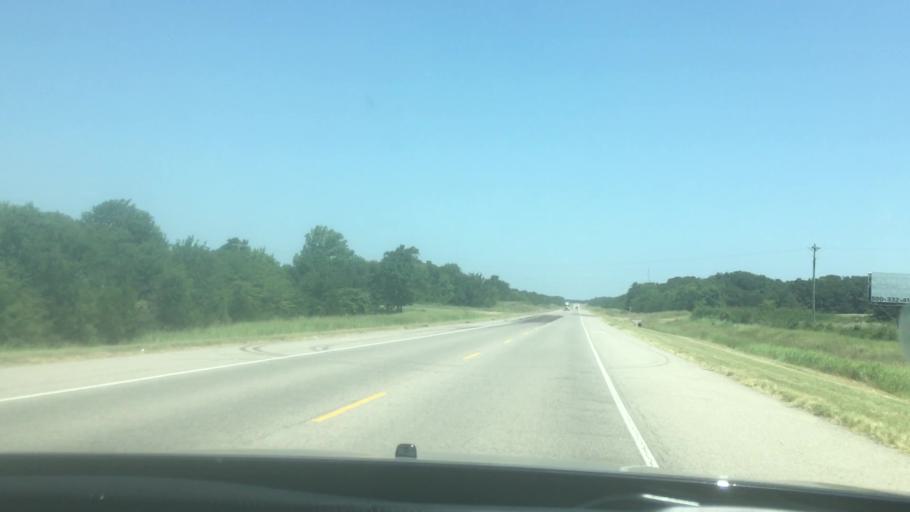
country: US
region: Oklahoma
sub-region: Pontotoc County
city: Ada
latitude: 34.6493
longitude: -96.5526
